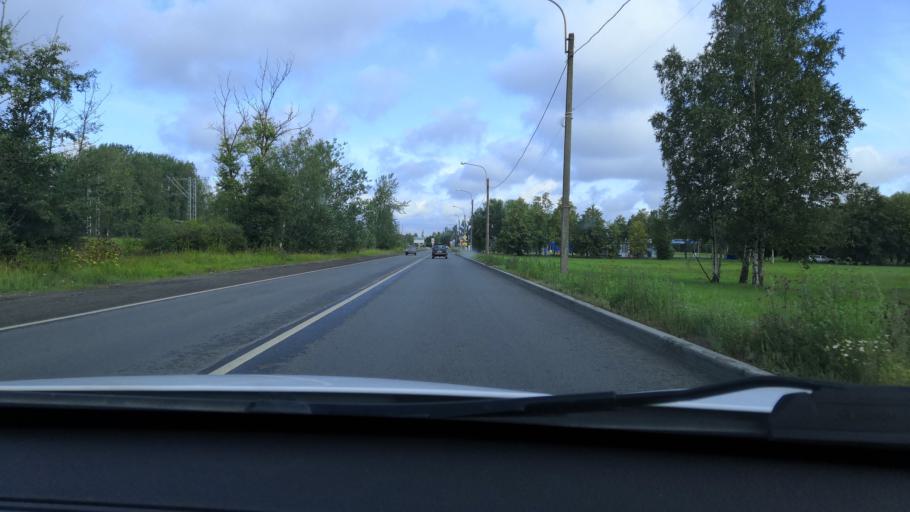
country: RU
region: St.-Petersburg
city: Tyarlevo
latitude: 59.7089
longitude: 30.4372
